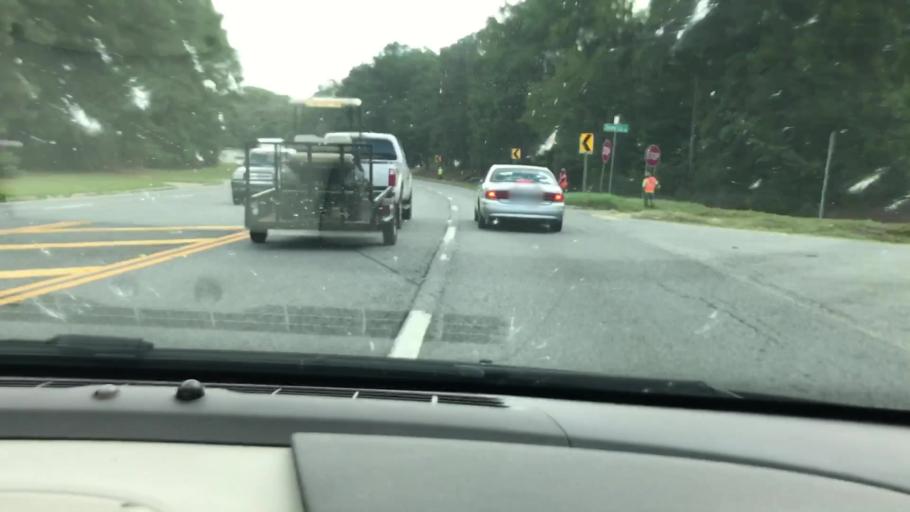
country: US
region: Georgia
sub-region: Tift County
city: Unionville
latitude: 31.4382
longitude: -83.5646
